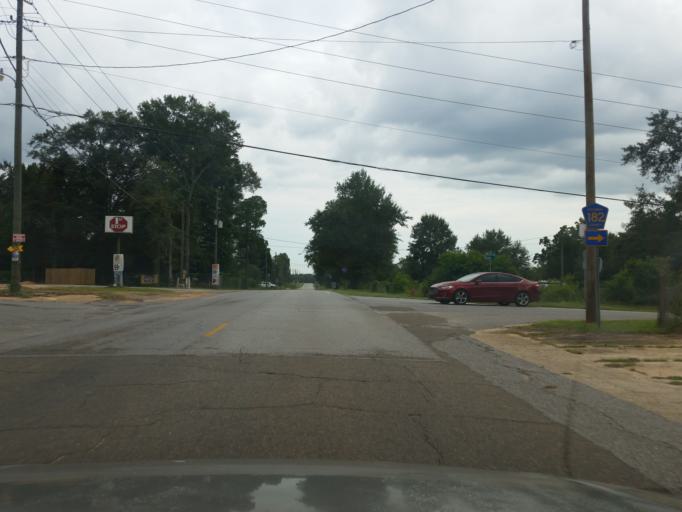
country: US
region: Florida
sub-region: Escambia County
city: Molino
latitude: 30.7180
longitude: -87.3388
